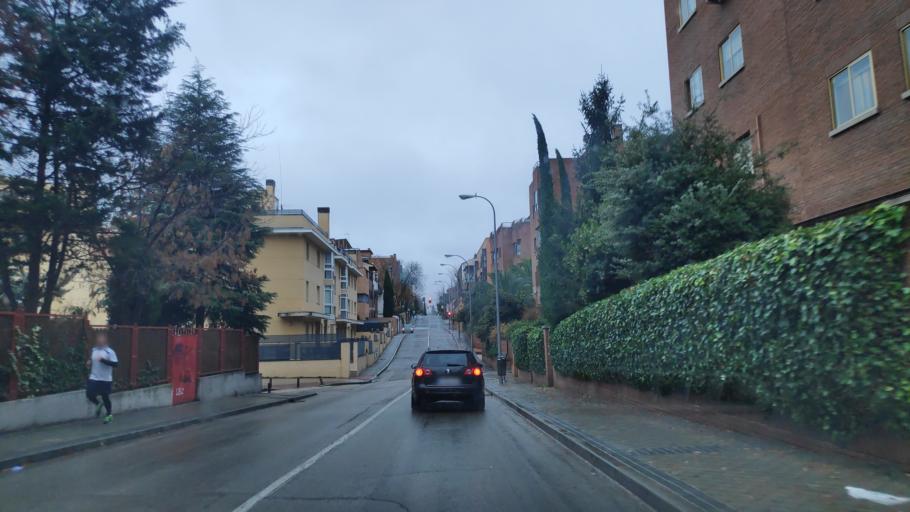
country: ES
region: Madrid
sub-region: Provincia de Madrid
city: Ciudad Lineal
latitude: 40.4565
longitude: -3.6538
